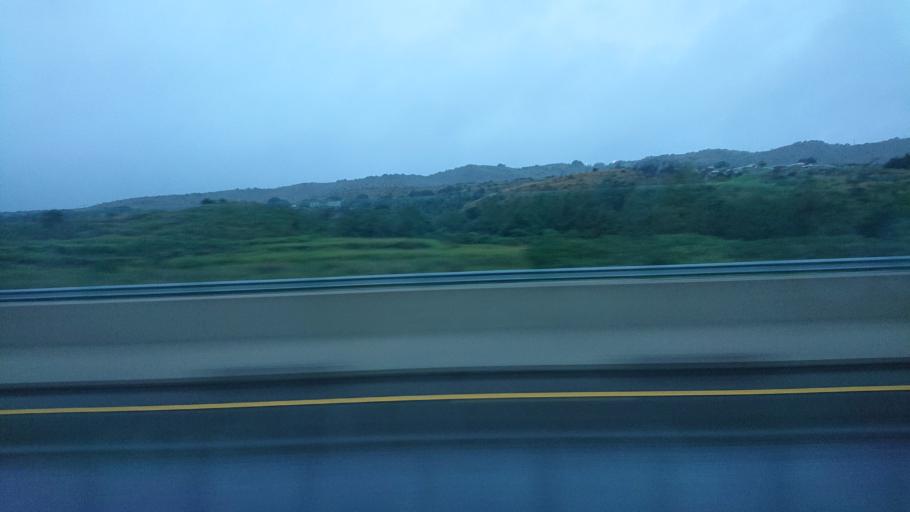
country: TW
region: Taiwan
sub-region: Miaoli
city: Miaoli
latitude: 24.5481
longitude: 120.7041
